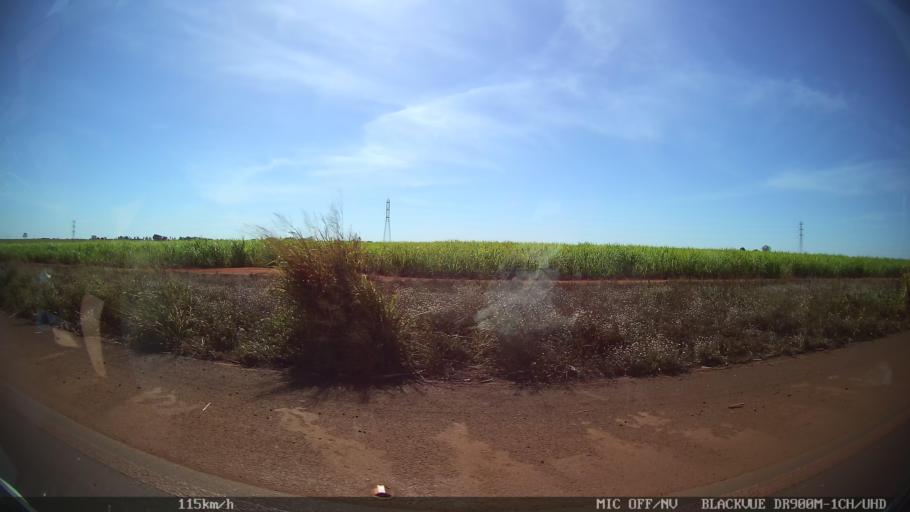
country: BR
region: Sao Paulo
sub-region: Guaira
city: Guaira
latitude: -20.4462
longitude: -48.4263
